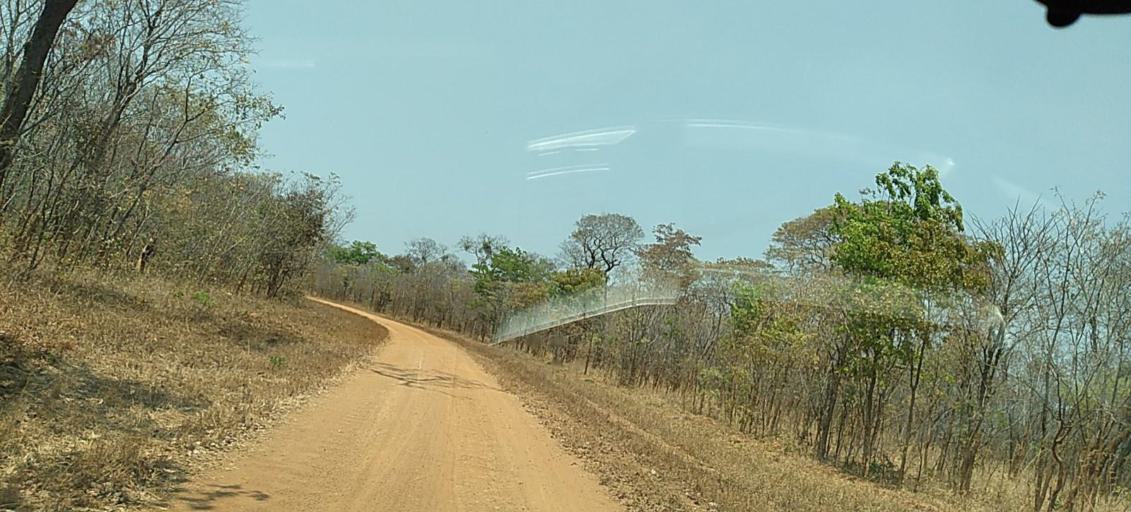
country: ZM
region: Central
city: Mumbwa
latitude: -14.3829
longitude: 26.4827
